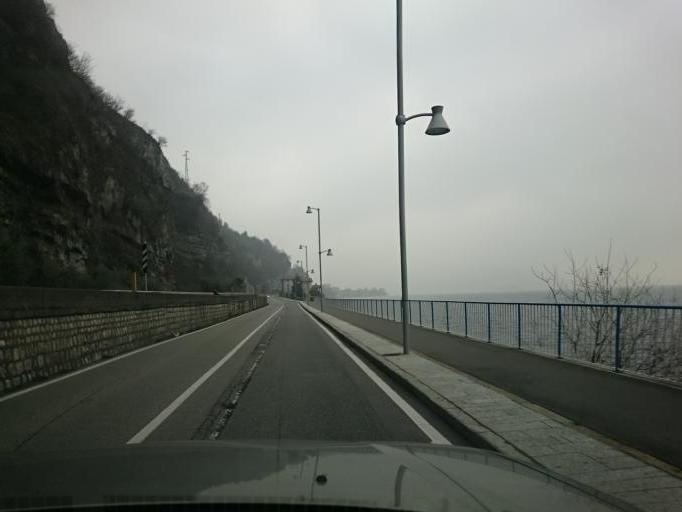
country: IT
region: Lombardy
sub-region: Provincia di Brescia
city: Marone
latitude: 45.7475
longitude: 10.0886
